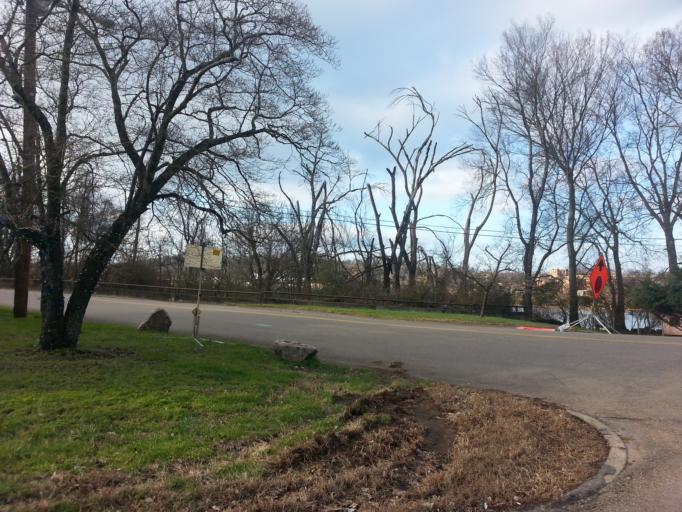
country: US
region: Tennessee
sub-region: Knox County
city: Knoxville
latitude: 35.9600
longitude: -83.8891
